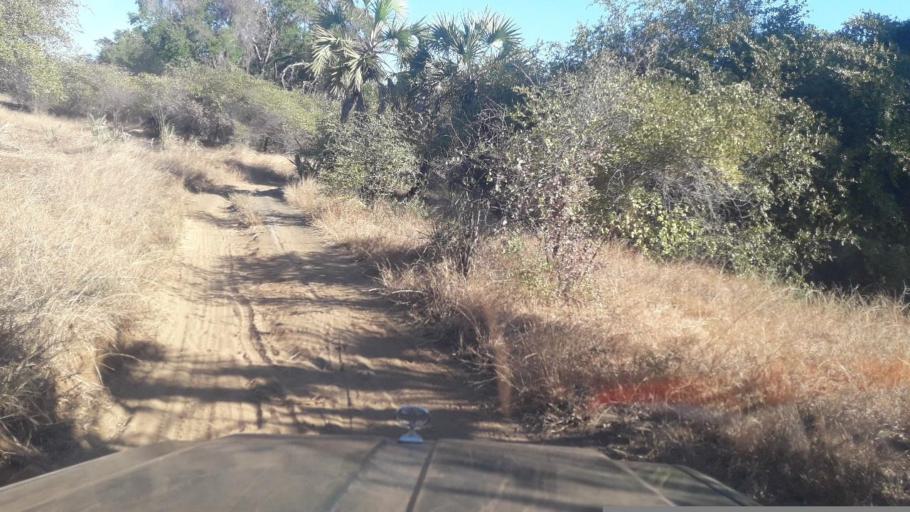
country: MG
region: Boeny
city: Sitampiky
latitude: -16.4007
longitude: 45.5983
